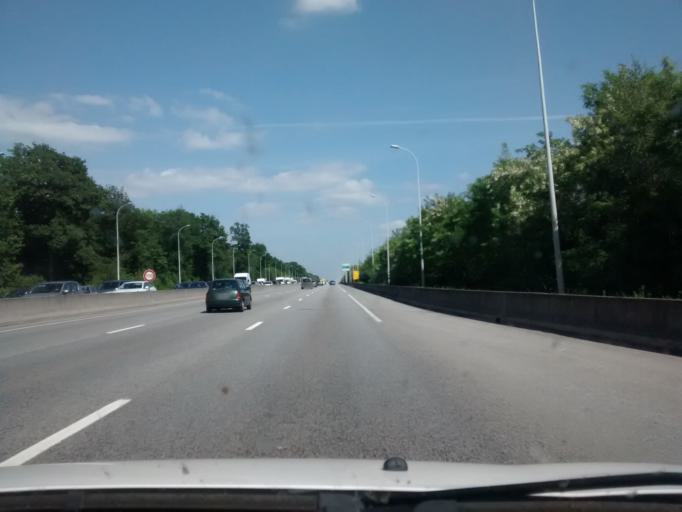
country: FR
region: Ile-de-France
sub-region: Departement des Yvelines
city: Saint-Cyr-l'Ecole
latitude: 48.7925
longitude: 2.0882
